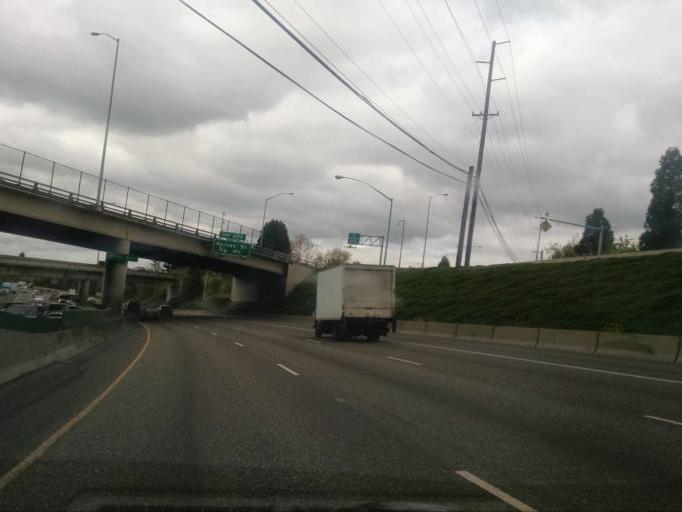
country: US
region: Oregon
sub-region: Washington County
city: Metzger
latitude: 45.4441
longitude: -122.7395
